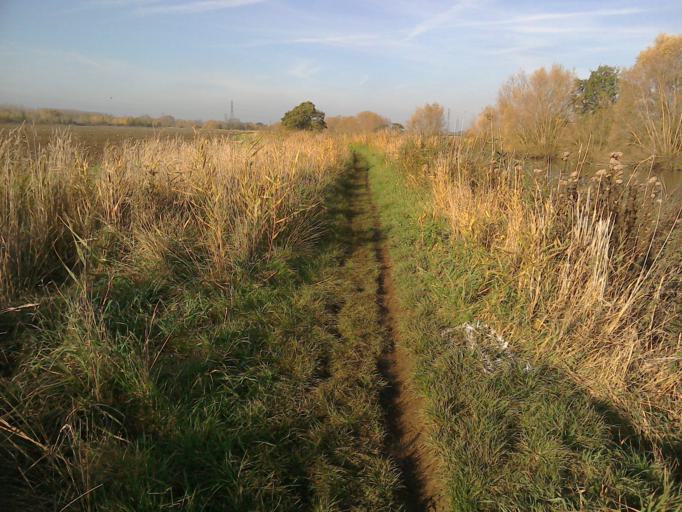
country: GB
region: England
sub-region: Oxfordshire
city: Radley
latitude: 51.6879
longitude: -1.2221
